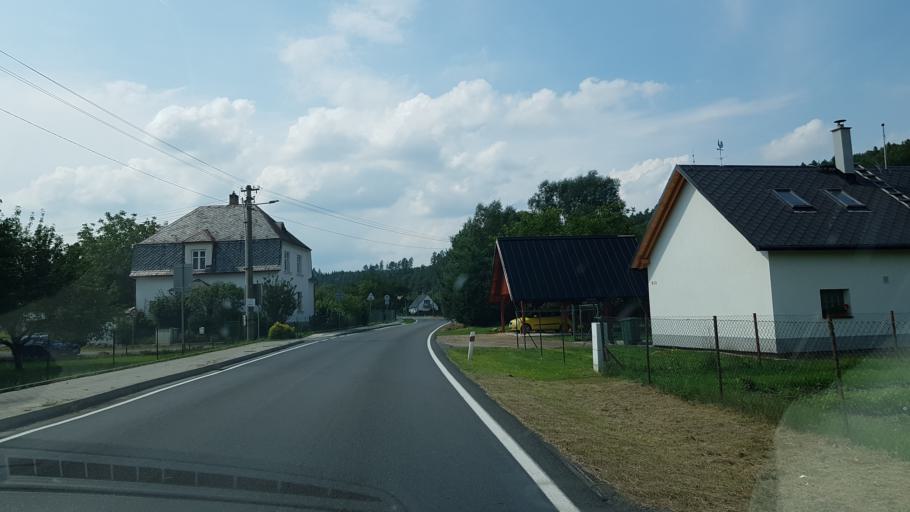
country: CZ
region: Olomoucky
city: Mikulovice
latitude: 50.2928
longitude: 17.3039
